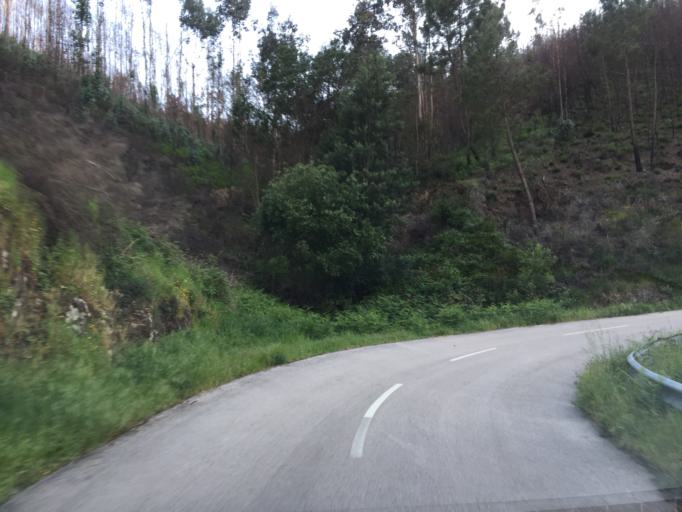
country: PT
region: Coimbra
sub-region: Pampilhosa da Serra
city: Pampilhosa da Serra
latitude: 40.1314
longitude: -8.0005
